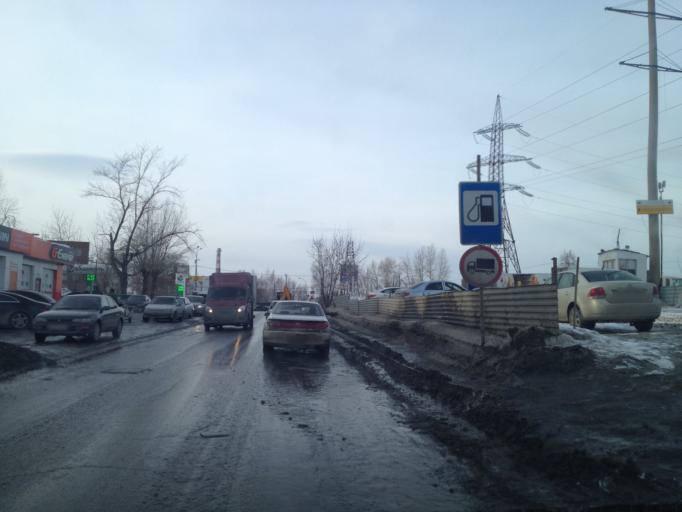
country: RU
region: Sverdlovsk
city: Yekaterinburg
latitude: 56.8747
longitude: 60.5558
